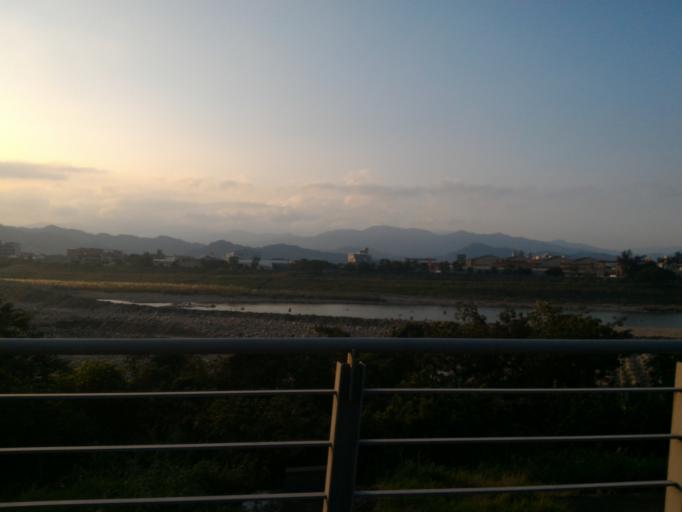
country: TW
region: Taiwan
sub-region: Taoyuan
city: Taoyuan
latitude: 24.9685
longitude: 121.3962
